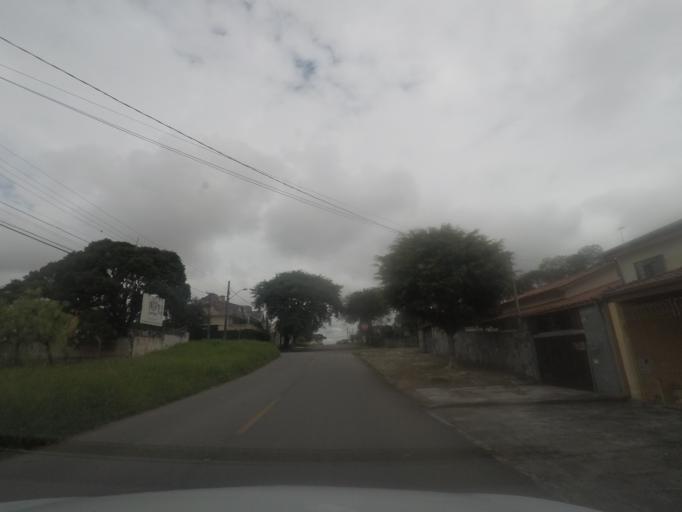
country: BR
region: Parana
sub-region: Pinhais
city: Pinhais
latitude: -25.4427
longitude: -49.2256
